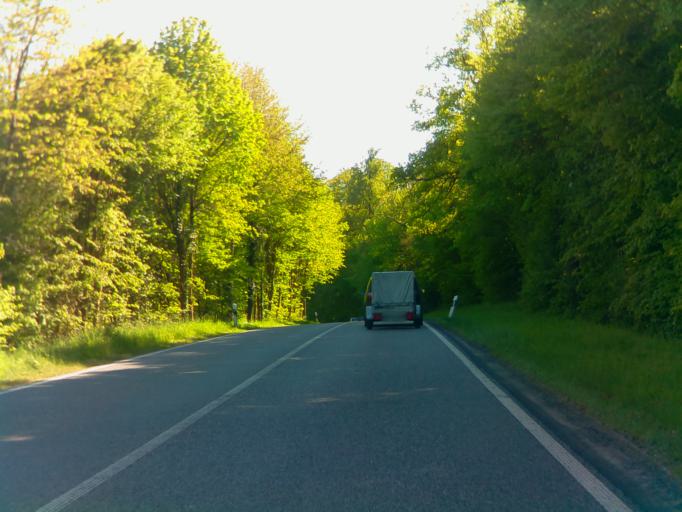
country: DE
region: Hesse
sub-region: Regierungsbezirk Darmstadt
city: Birstein
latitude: 50.3298
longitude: 9.2882
